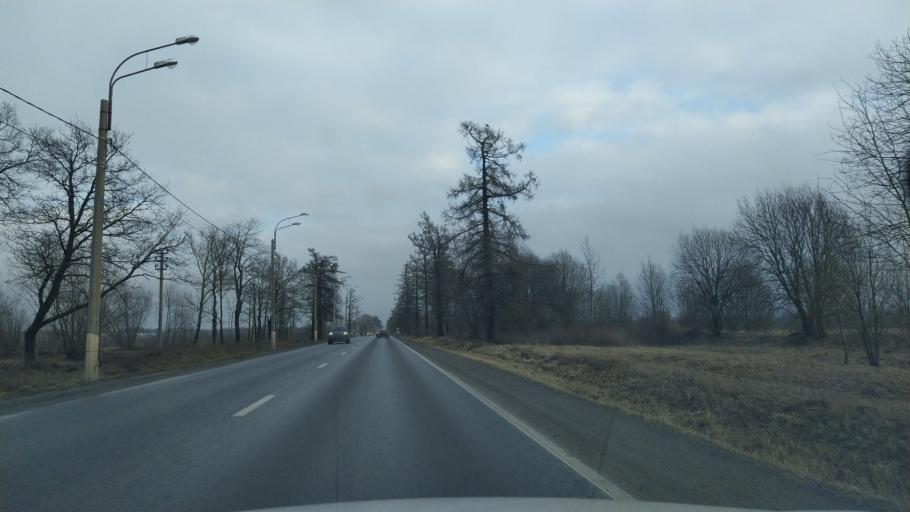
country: RU
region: St.-Petersburg
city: Aleksandrovskaya
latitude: 59.7101
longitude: 30.3198
